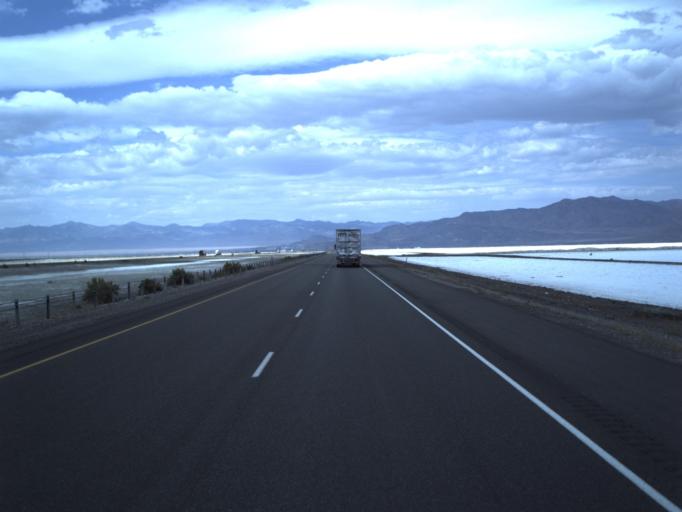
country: US
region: Utah
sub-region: Tooele County
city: Wendover
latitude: 40.7404
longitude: -113.9036
